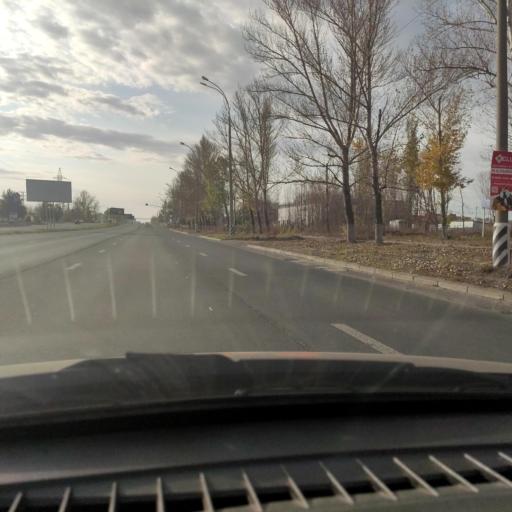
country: RU
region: Samara
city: Tol'yatti
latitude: 53.5482
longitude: 49.2862
